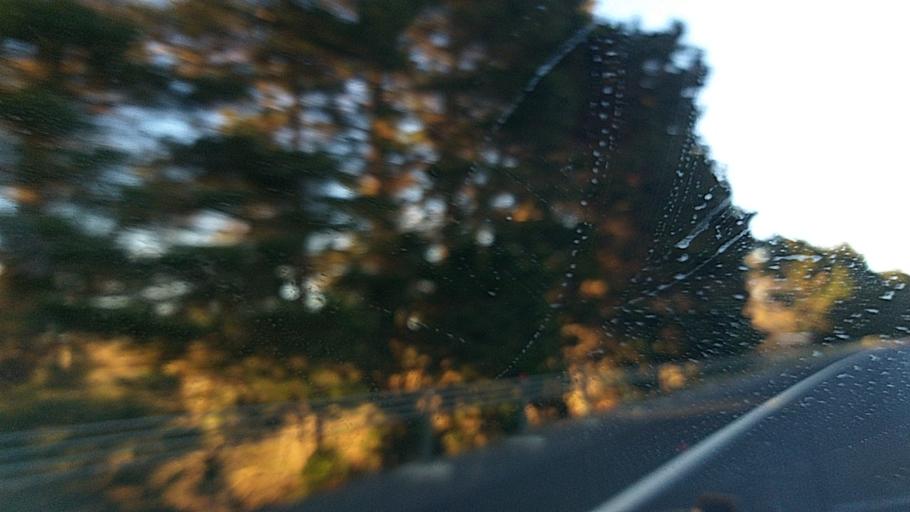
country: AU
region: New South Wales
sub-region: Goulburn Mulwaree
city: Goulburn
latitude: -34.8912
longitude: 149.5270
